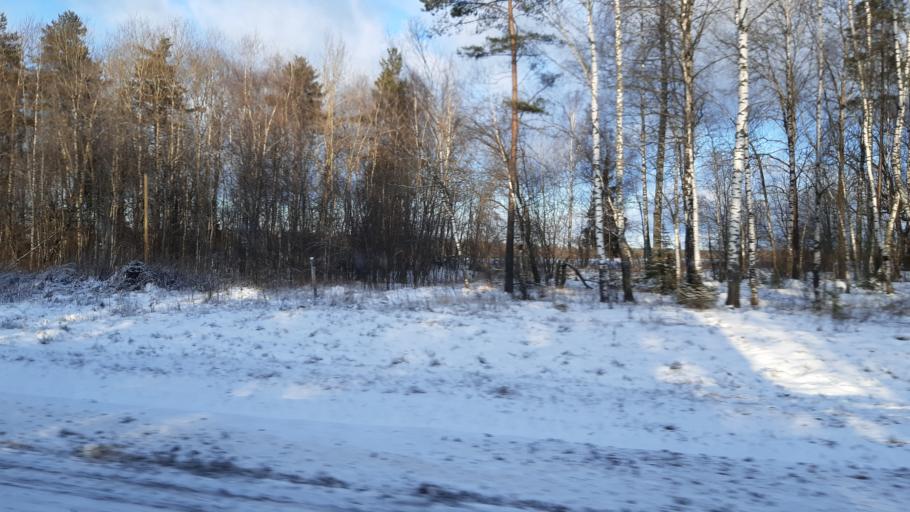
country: RU
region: Moskovskaya
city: Svatkovo
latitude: 56.3079
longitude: 38.3268
